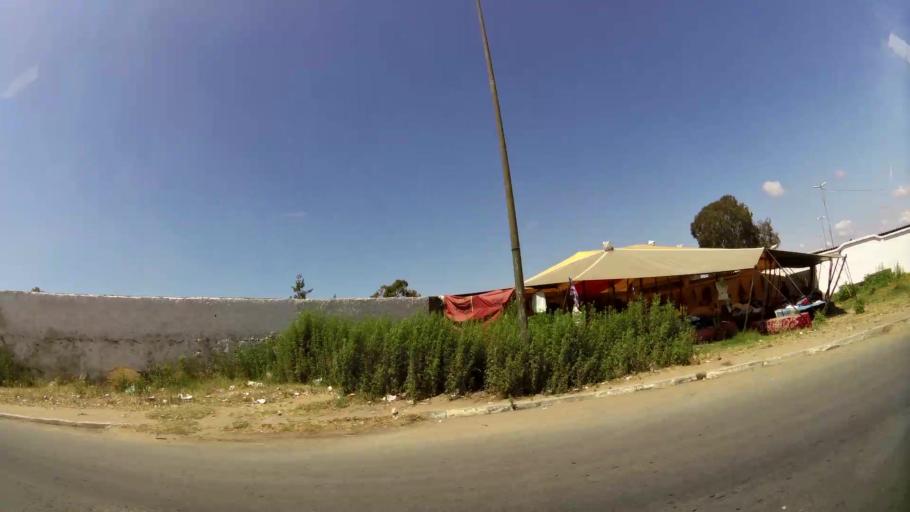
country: MA
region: Gharb-Chrarda-Beni Hssen
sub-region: Kenitra Province
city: Kenitra
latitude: 34.2505
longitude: -6.5390
